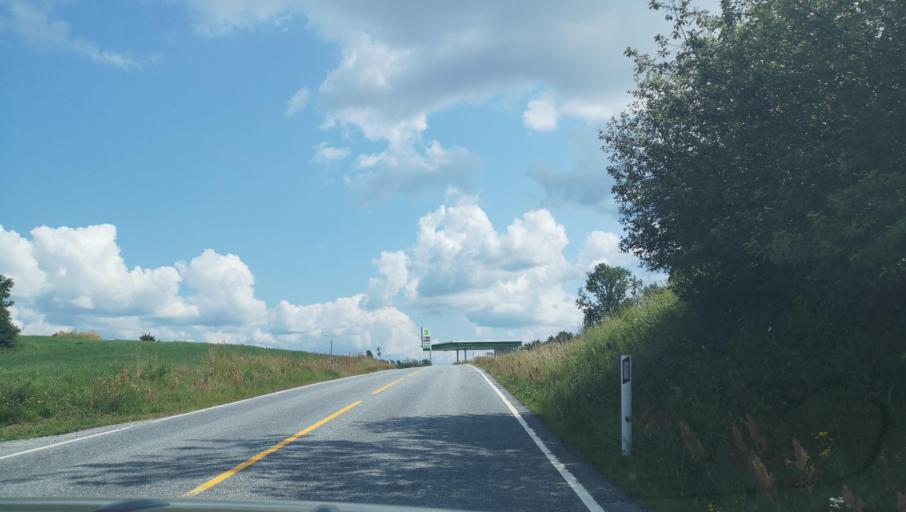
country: NO
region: Buskerud
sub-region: Ovre Eiker
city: Hokksund
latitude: 59.7294
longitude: 9.8409
